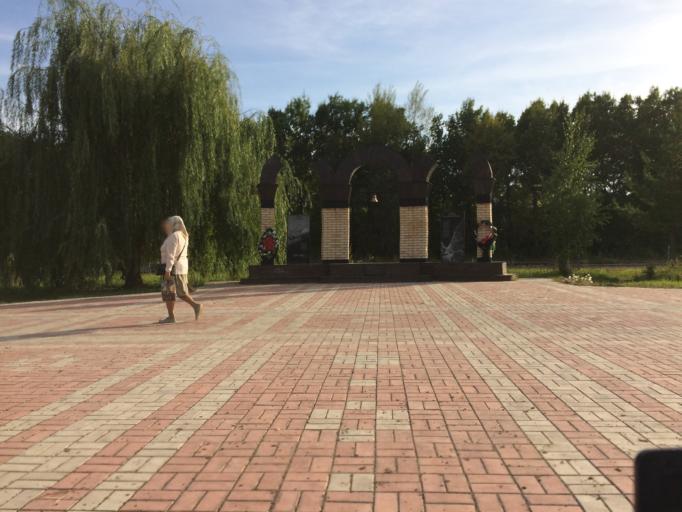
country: RU
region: Mariy-El
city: Medvedevo
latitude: 56.6280
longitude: 47.8115
